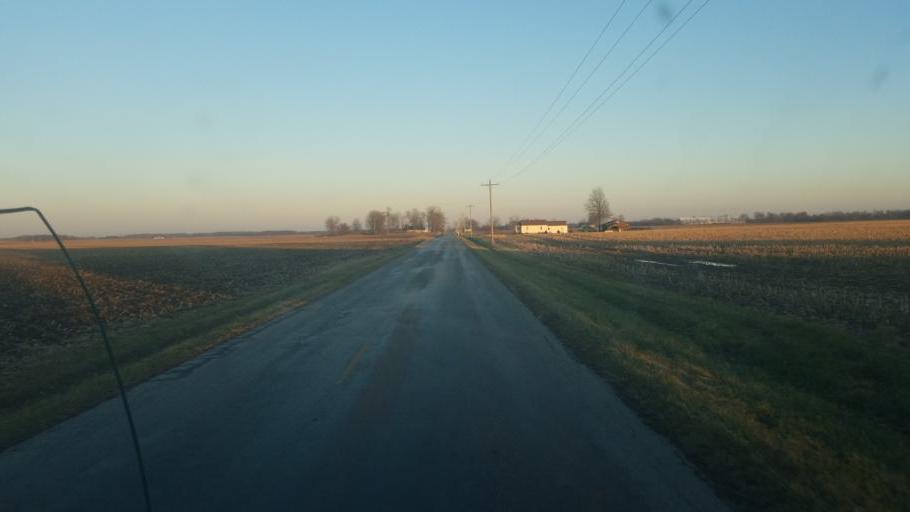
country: US
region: Ohio
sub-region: Union County
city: Richwood
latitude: 40.6220
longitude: -83.3558
